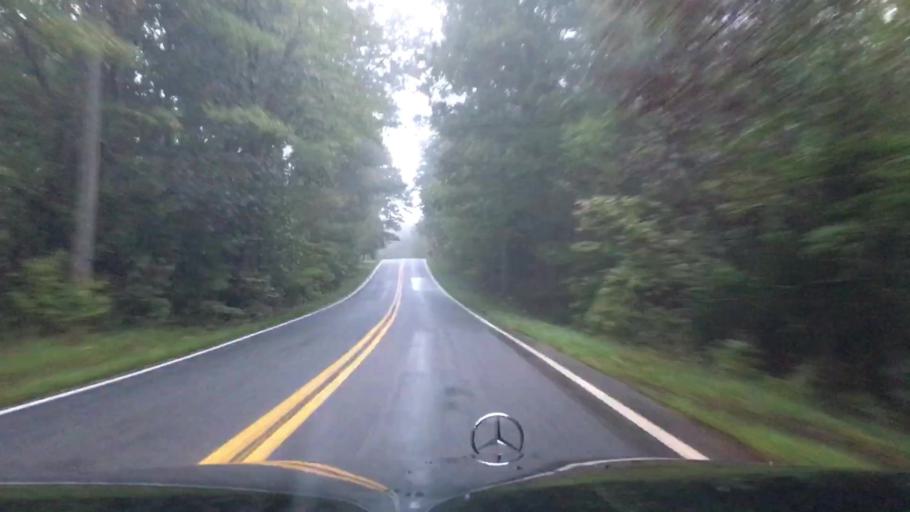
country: US
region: Virginia
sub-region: Campbell County
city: Timberlake
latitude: 37.2506
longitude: -79.2797
